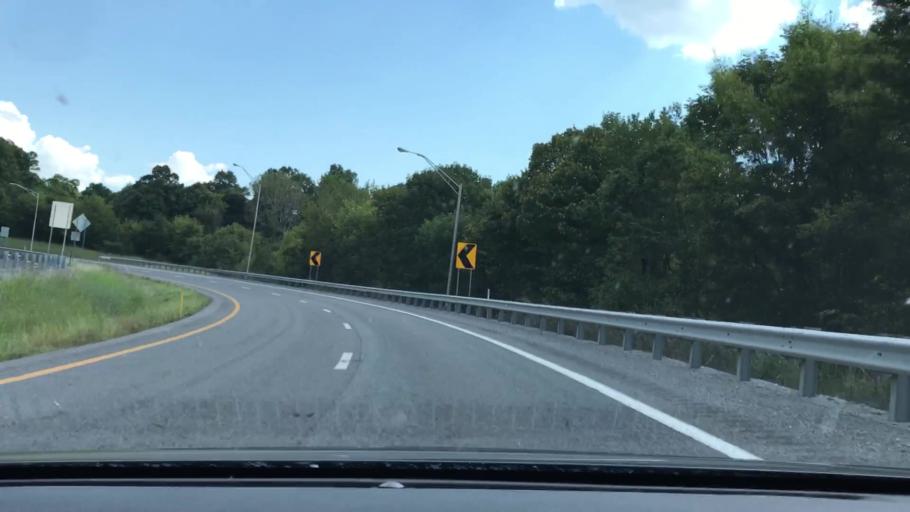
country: US
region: Kentucky
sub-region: Lyon County
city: Eddyville
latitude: 37.0705
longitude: -88.0887
